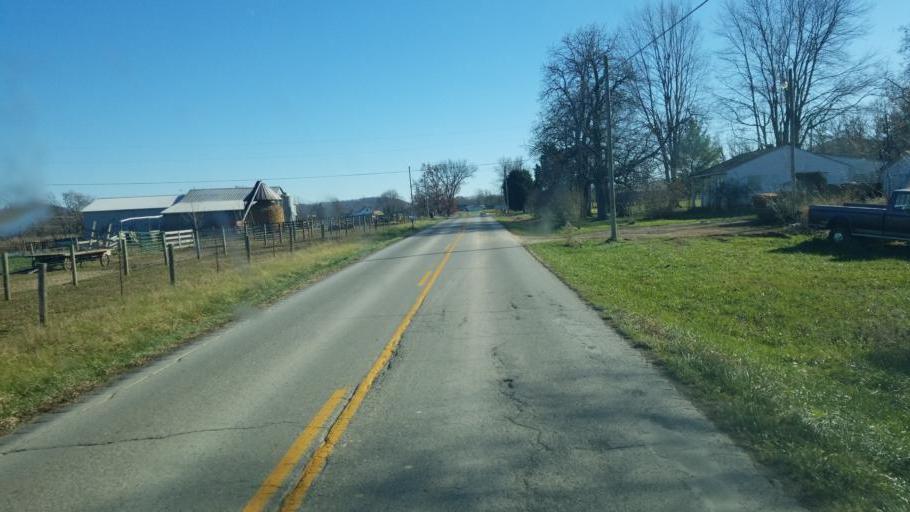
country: US
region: Kentucky
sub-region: Fleming County
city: Flemingsburg
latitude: 38.4815
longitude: -83.6084
